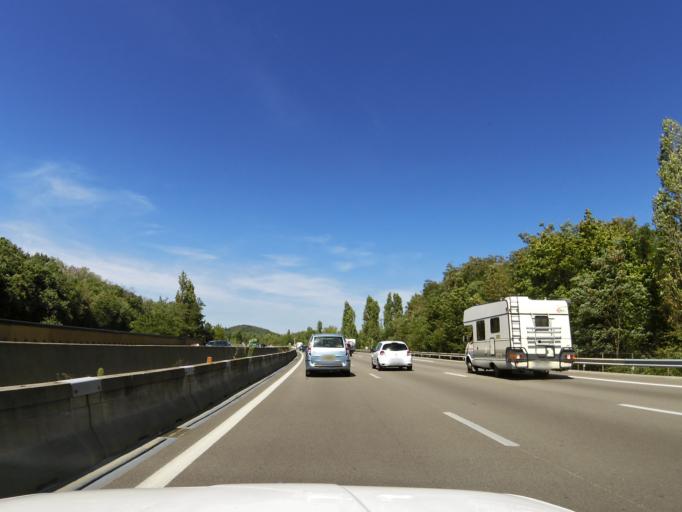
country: FR
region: Rhone-Alpes
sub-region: Departement de la Drome
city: Mercurol
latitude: 45.1236
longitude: 4.8966
